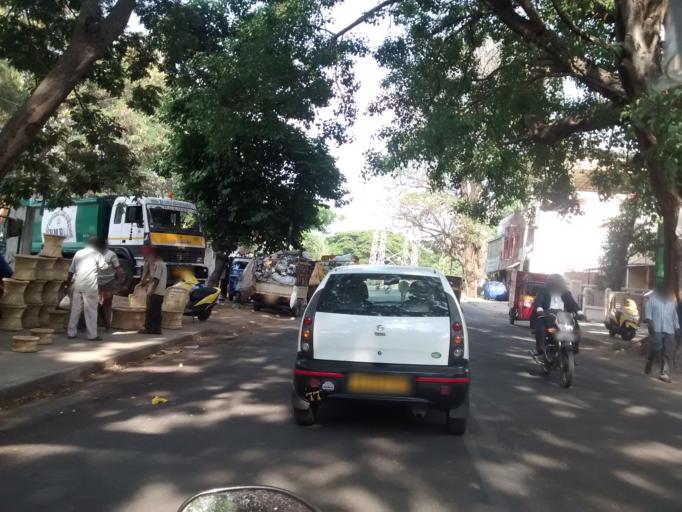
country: IN
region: Karnataka
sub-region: Bangalore Urban
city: Bangalore
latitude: 12.9671
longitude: 77.6588
